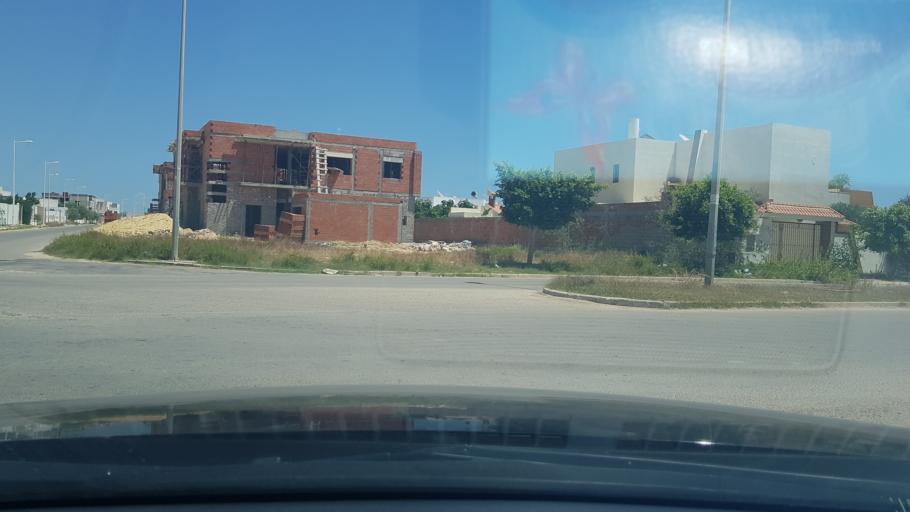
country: TN
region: Safaqis
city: Al Qarmadah
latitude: 34.8380
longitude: 10.7590
